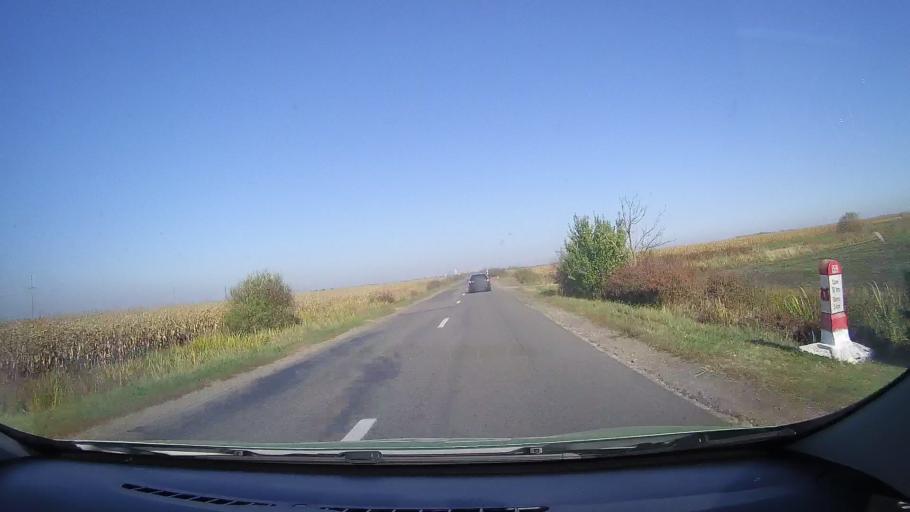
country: RO
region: Satu Mare
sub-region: Comuna Cauas
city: Cauas
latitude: 47.6115
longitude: 22.5388
